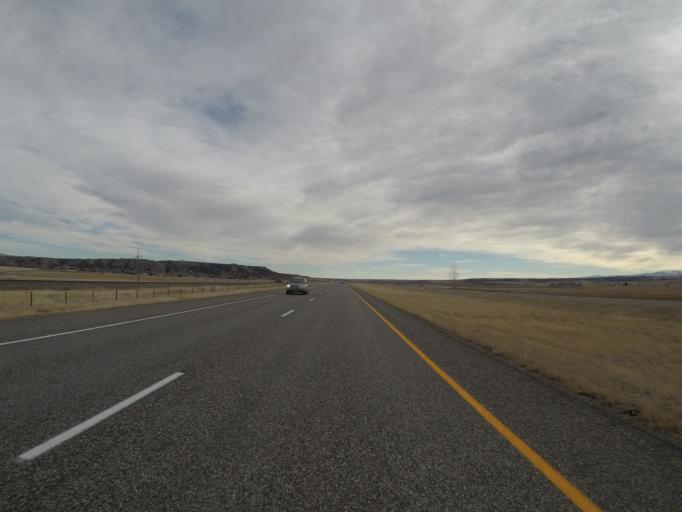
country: US
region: Montana
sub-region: Sweet Grass County
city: Big Timber
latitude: 45.8244
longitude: -109.8825
